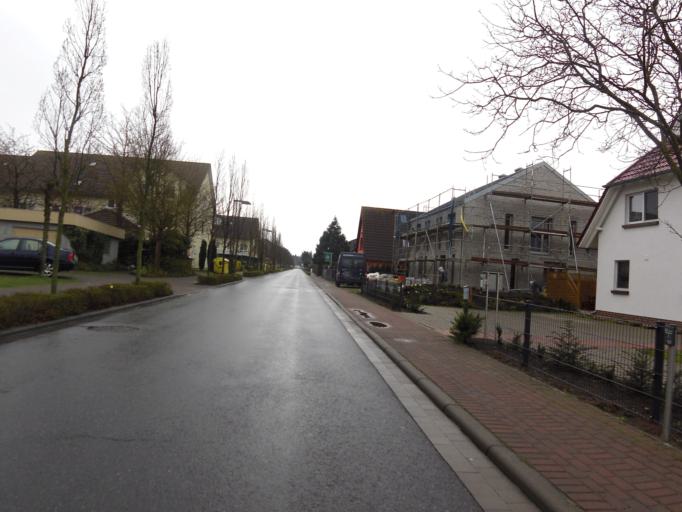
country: DE
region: Mecklenburg-Vorpommern
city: Zingst
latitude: 54.4388
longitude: 12.7013
